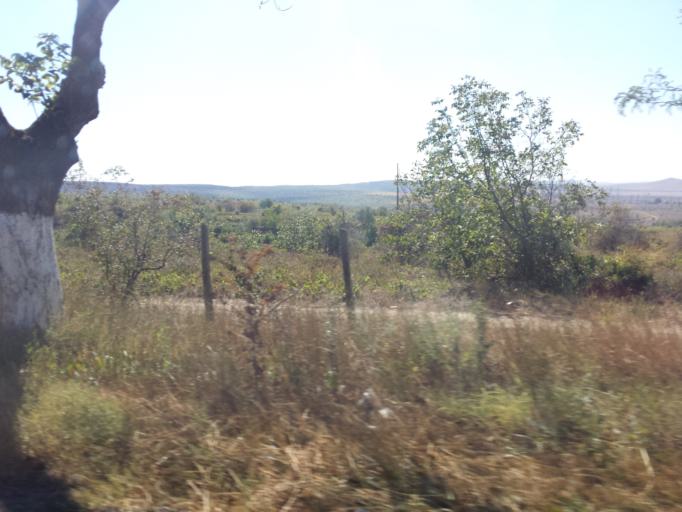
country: RO
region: Tulcea
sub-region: Municipiul Tulcea
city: Tulcea
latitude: 45.1555
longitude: 28.7852
